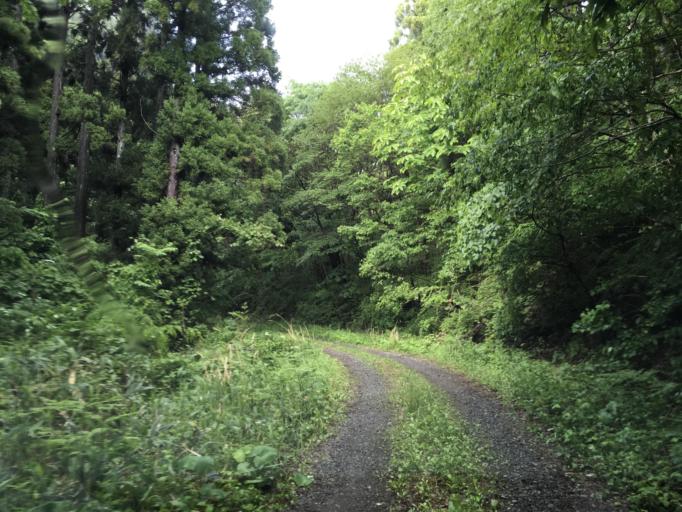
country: JP
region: Iwate
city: Ichinoseki
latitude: 38.8681
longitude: 141.4472
